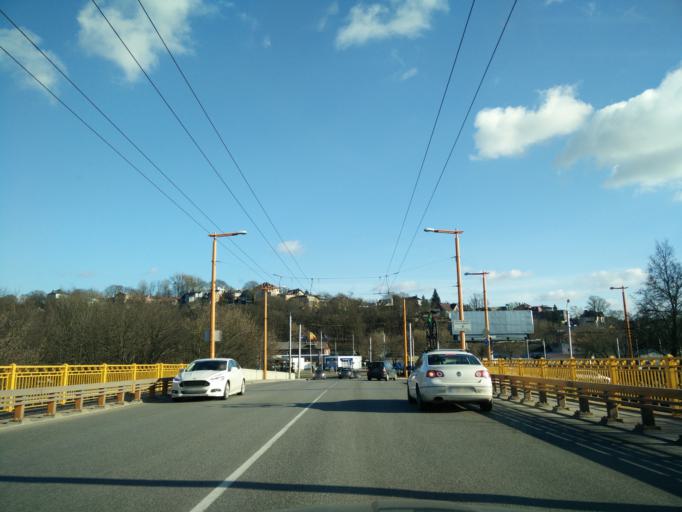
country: LT
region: Kauno apskritis
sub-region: Kaunas
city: Kaunas
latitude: 54.9025
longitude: 23.8923
